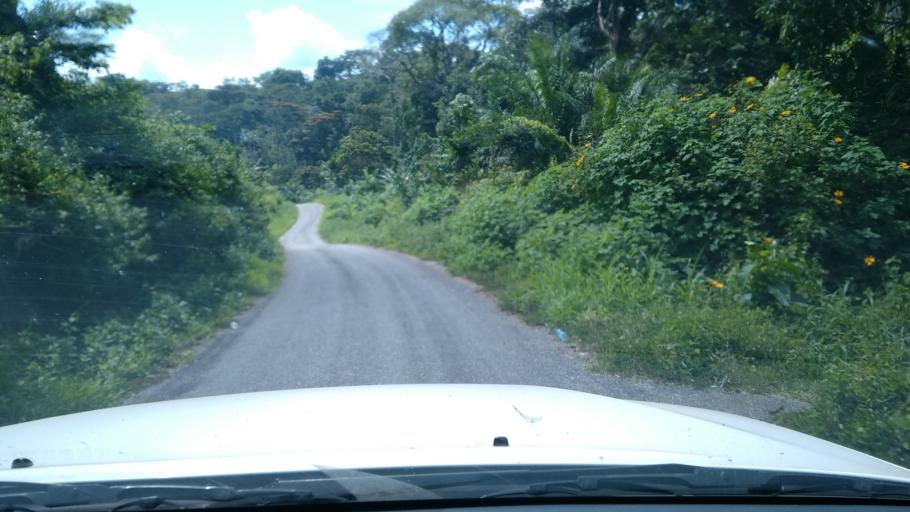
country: CM
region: Centre
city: Evodoula
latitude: 4.1471
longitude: 11.2827
